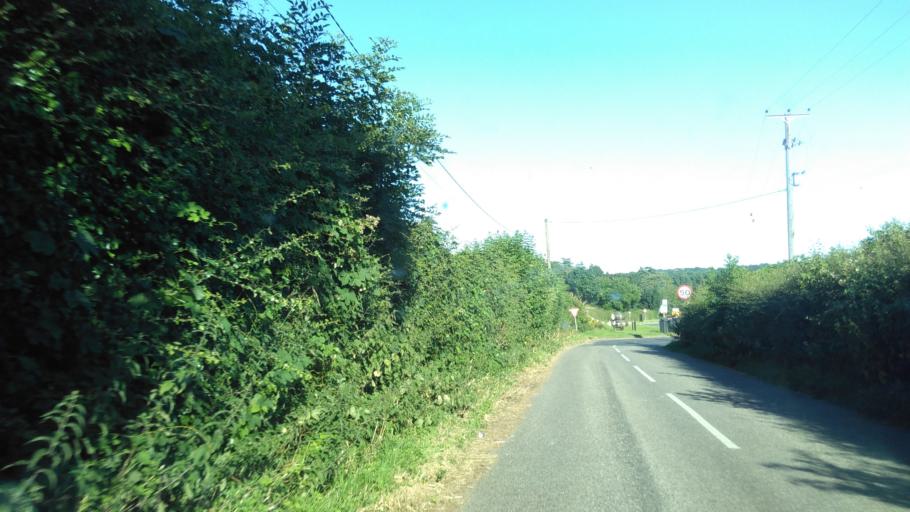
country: GB
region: England
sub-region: Kent
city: Dunkirk
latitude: 51.2466
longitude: 0.9660
